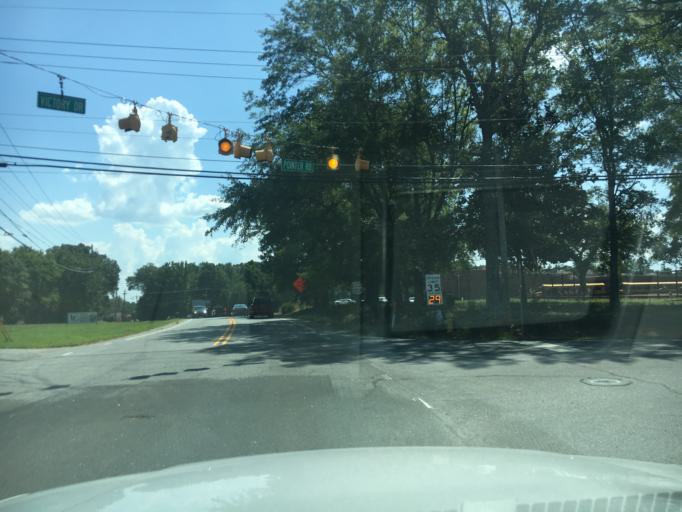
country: US
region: North Carolina
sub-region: Rutherford County
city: Forest City
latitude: 35.3076
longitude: -81.8586
